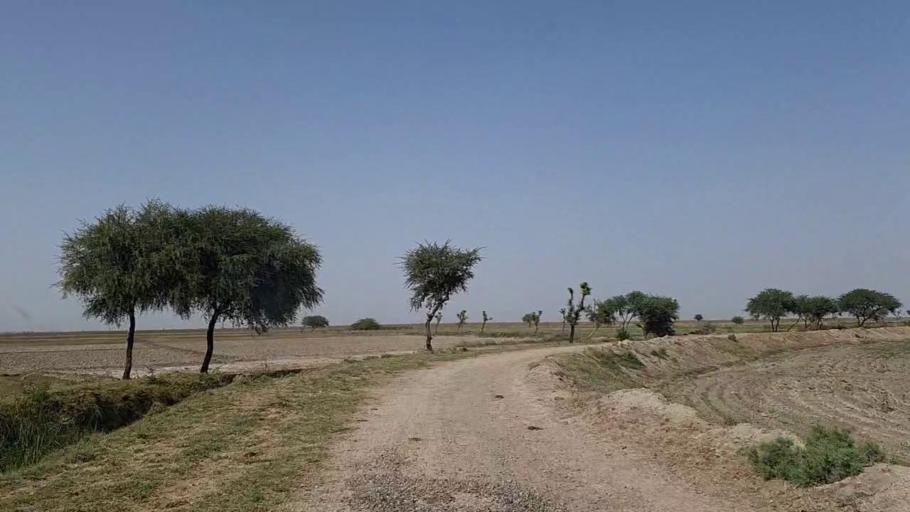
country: PK
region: Sindh
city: Jati
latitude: 24.3510
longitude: 68.3143
